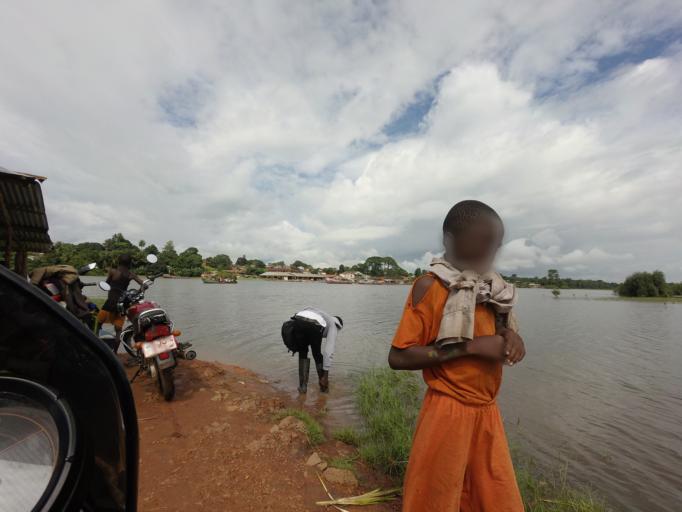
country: SL
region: Northern Province
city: Mambolo
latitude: 9.0059
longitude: -12.9564
